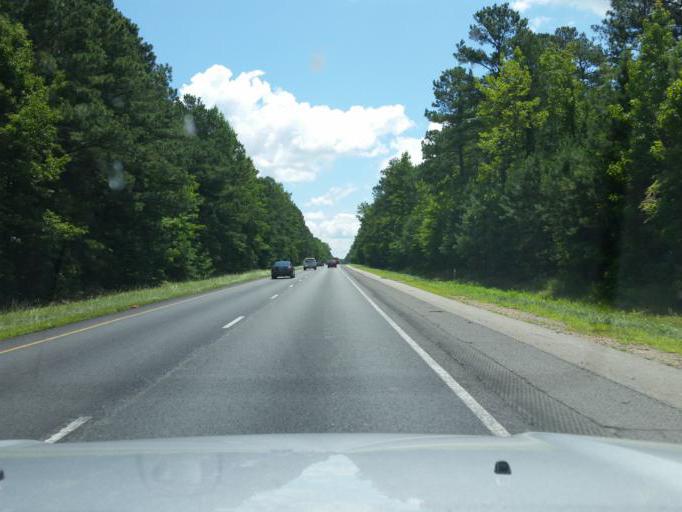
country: US
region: Virginia
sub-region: New Kent County
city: New Kent
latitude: 37.4870
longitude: -76.9624
